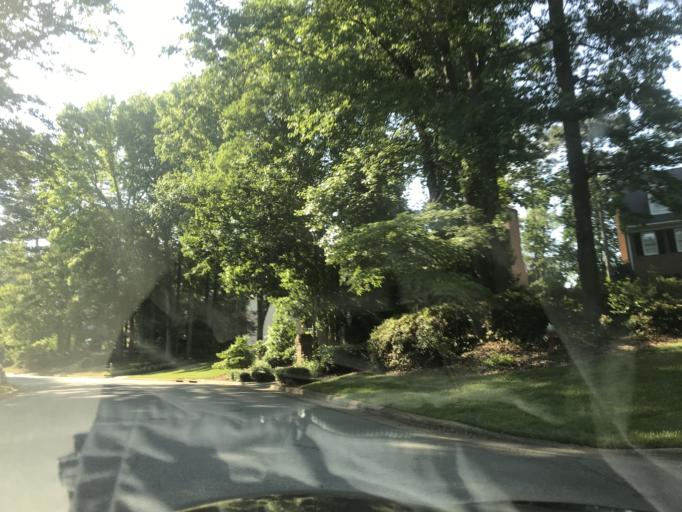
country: US
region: North Carolina
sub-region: Wake County
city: West Raleigh
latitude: 35.8829
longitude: -78.6028
